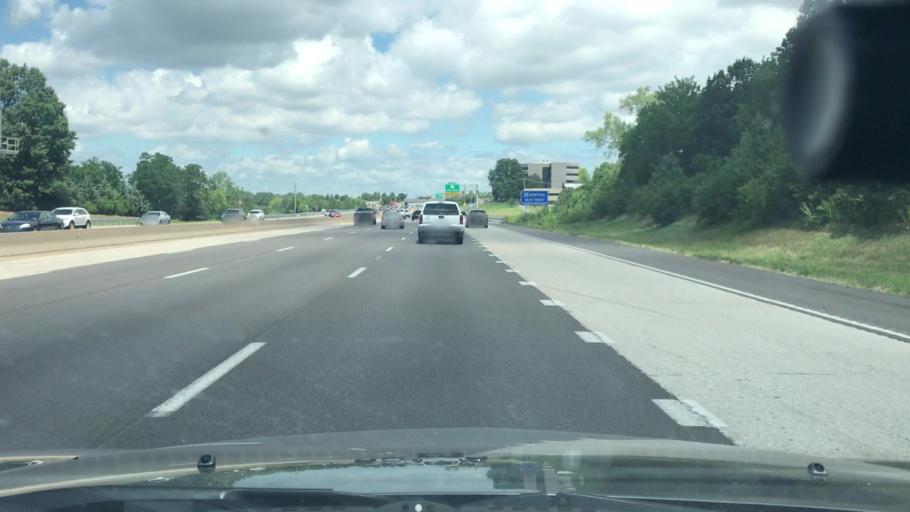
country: US
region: Missouri
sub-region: Saint Louis County
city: Creve Coeur
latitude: 38.6641
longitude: -90.4485
